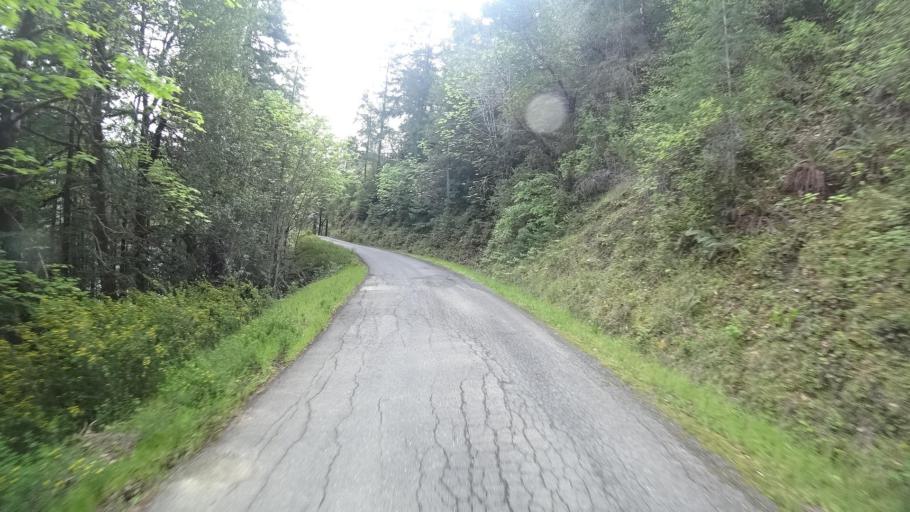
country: US
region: California
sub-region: Humboldt County
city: Redway
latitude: 40.3390
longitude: -123.8684
